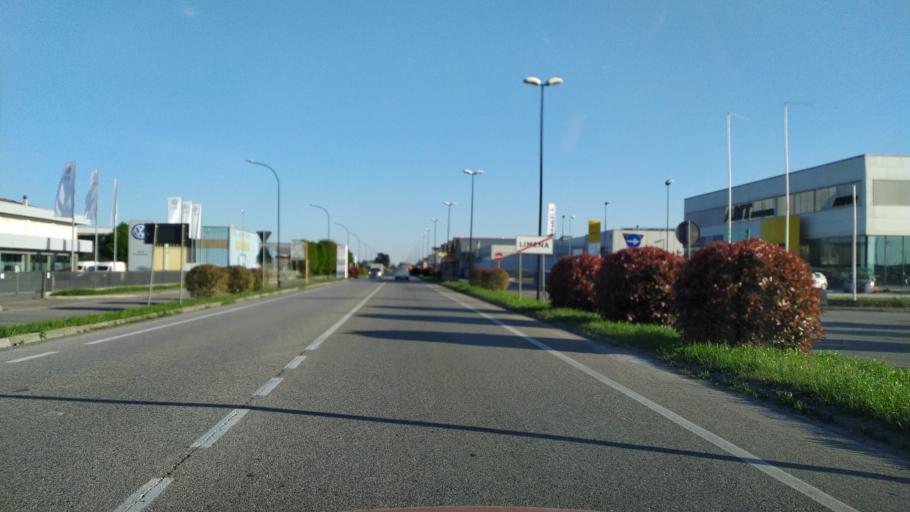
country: IT
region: Veneto
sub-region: Provincia di Padova
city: Limena
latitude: 45.4636
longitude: 11.8522
